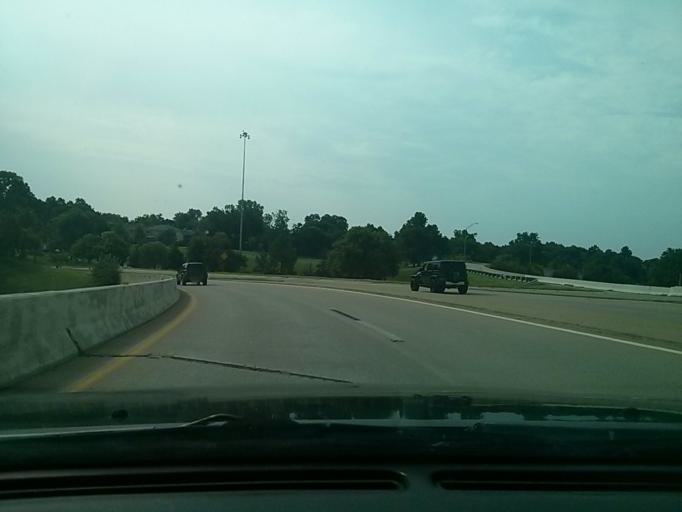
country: US
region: Oklahoma
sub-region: Tulsa County
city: Tulsa
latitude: 36.1420
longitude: -95.9829
